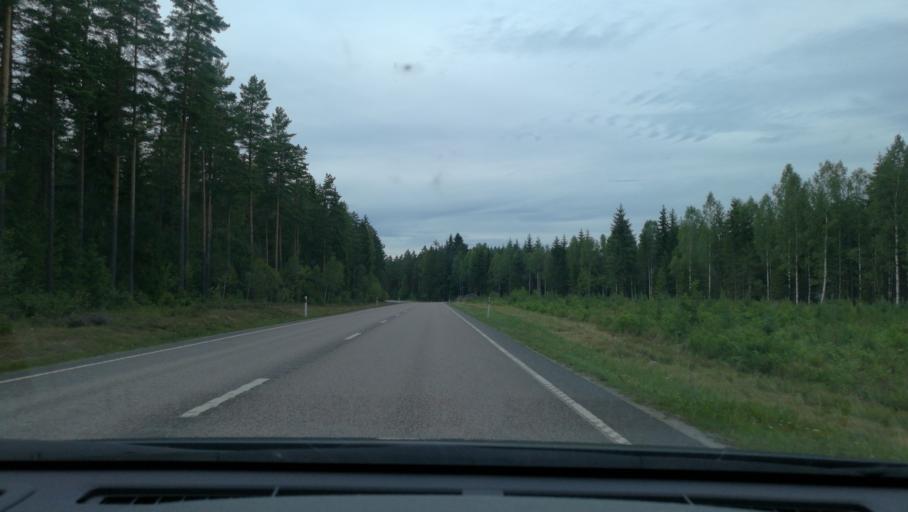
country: SE
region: Vaestmanland
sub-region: Kungsors Kommun
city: Kungsoer
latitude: 59.2084
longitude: 16.1021
